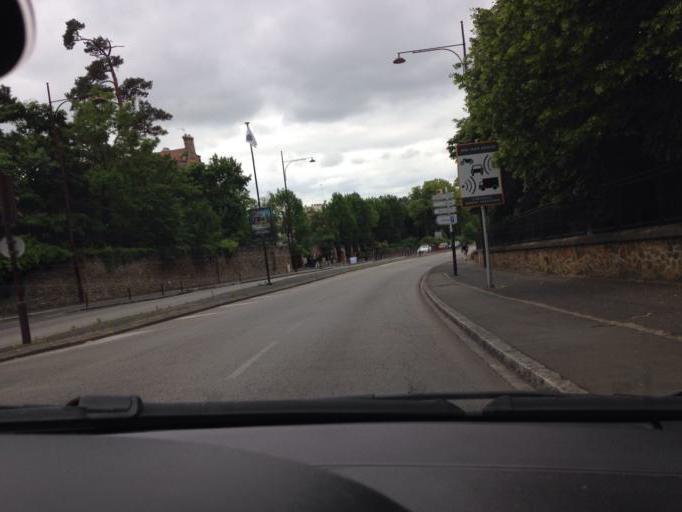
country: FR
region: Ile-de-France
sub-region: Departement des Yvelines
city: Viroflay
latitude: 48.8110
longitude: 2.1504
